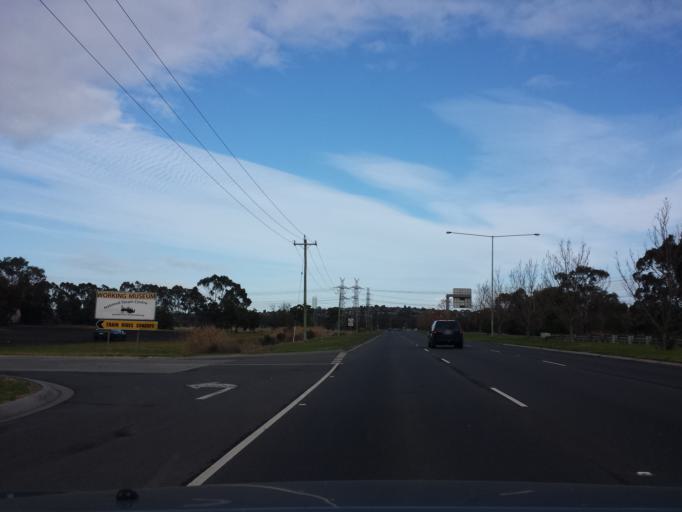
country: AU
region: Victoria
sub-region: Monash
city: Mulgrave
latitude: -37.9044
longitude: 145.2133
